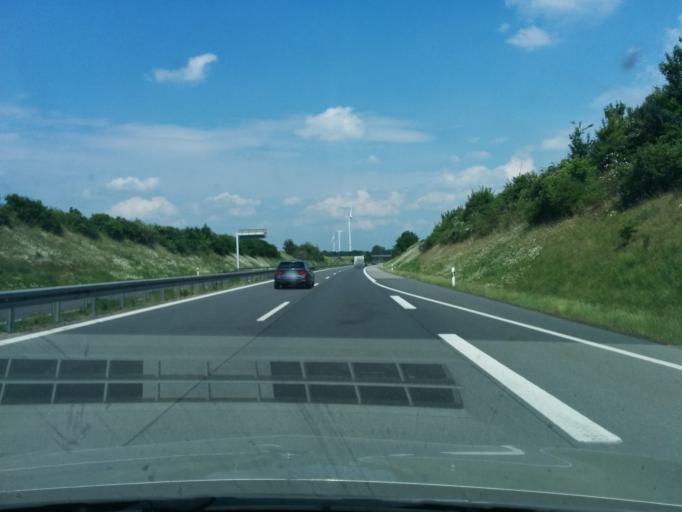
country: DE
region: Brandenburg
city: Schenkenberg
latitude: 53.3582
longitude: 13.9746
